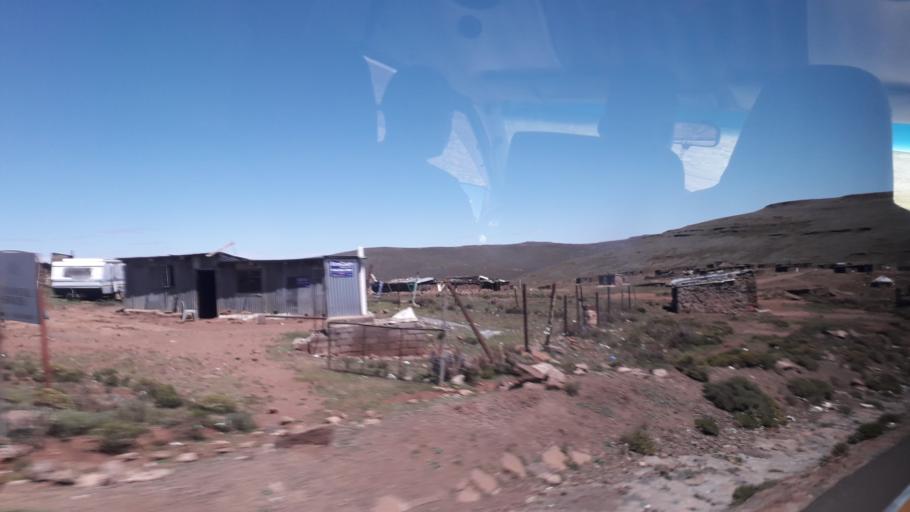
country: LS
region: Mokhotlong
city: Mokhotlong
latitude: -29.0141
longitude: 28.8446
